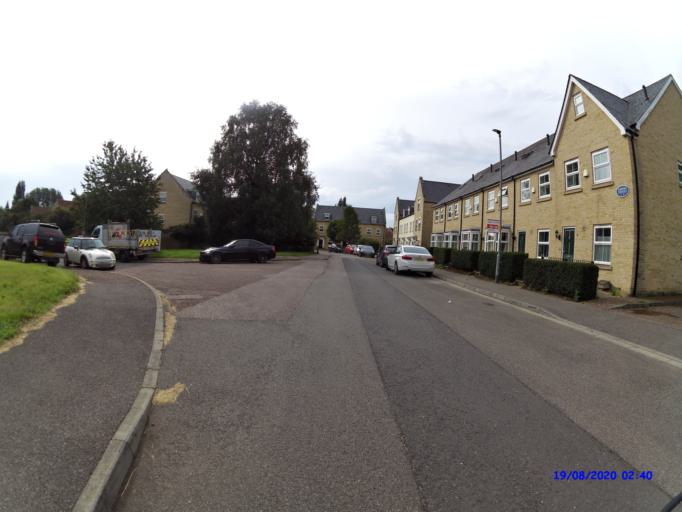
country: GB
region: England
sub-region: Cambridgeshire
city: Ramsey
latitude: 52.4451
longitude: -0.1106
